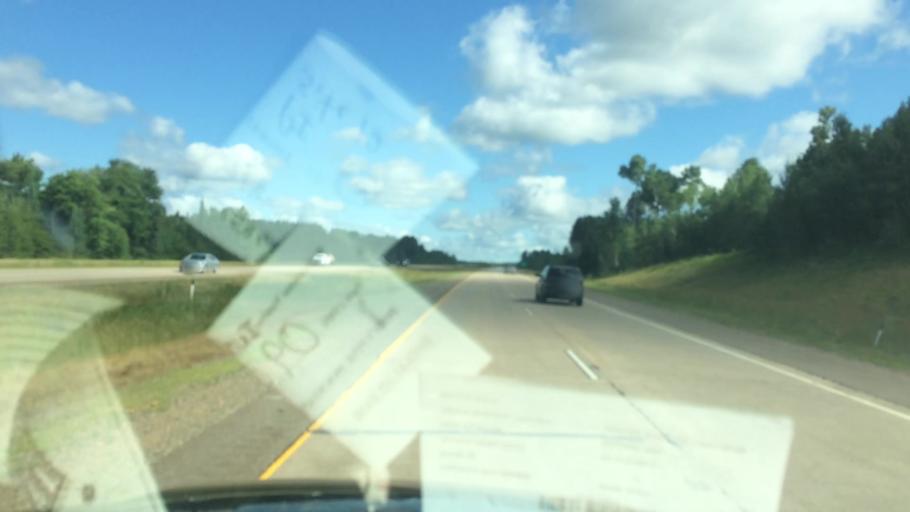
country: US
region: Wisconsin
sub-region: Lincoln County
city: Tomahawk
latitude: 45.3990
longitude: -89.6721
